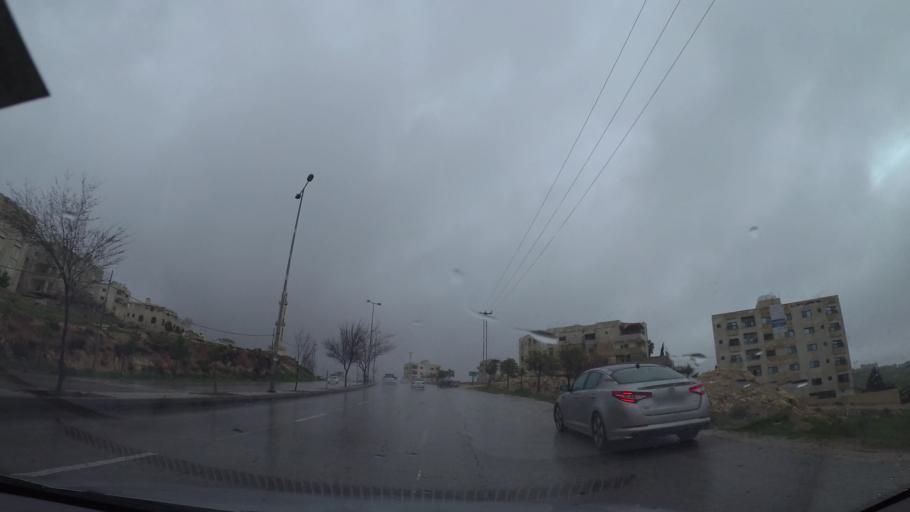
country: JO
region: Amman
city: Al Jubayhah
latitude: 32.0358
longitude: 35.8930
